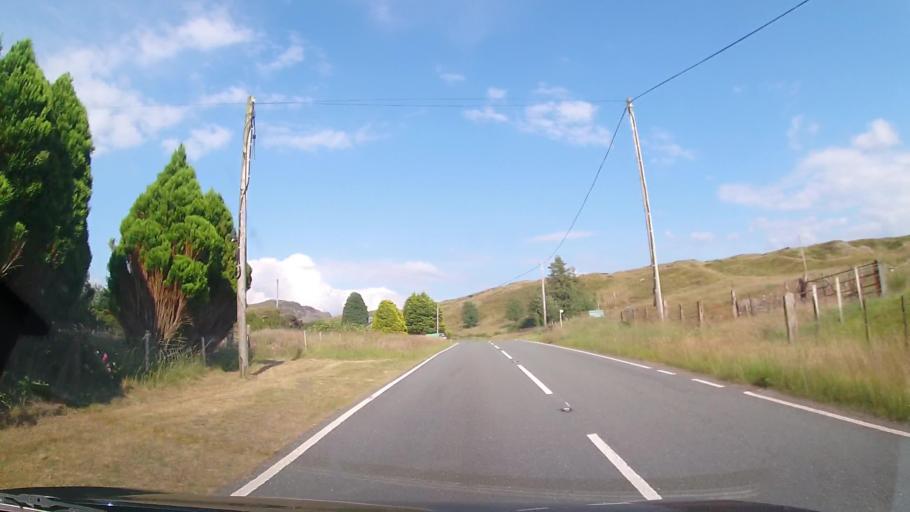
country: GB
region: Wales
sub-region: Gwynedd
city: Ffestiniog
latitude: 52.9620
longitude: -3.9167
